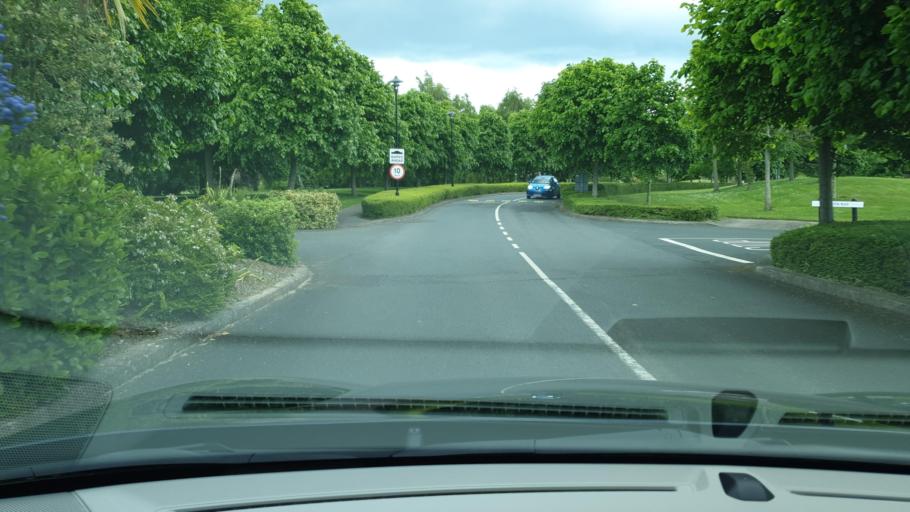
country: IE
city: Kilquade
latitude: 53.0919
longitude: -6.0843
